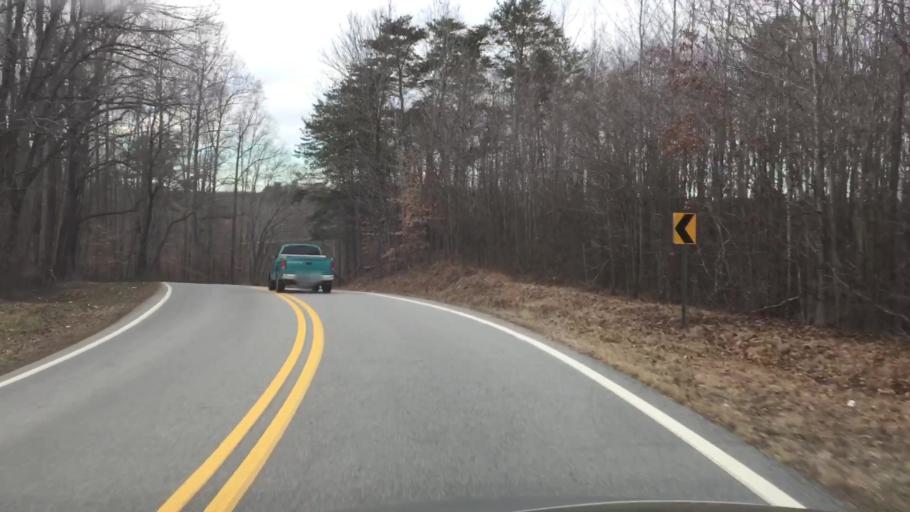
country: US
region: North Carolina
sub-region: Rockingham County
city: Reidsville
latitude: 36.3940
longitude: -79.6578
